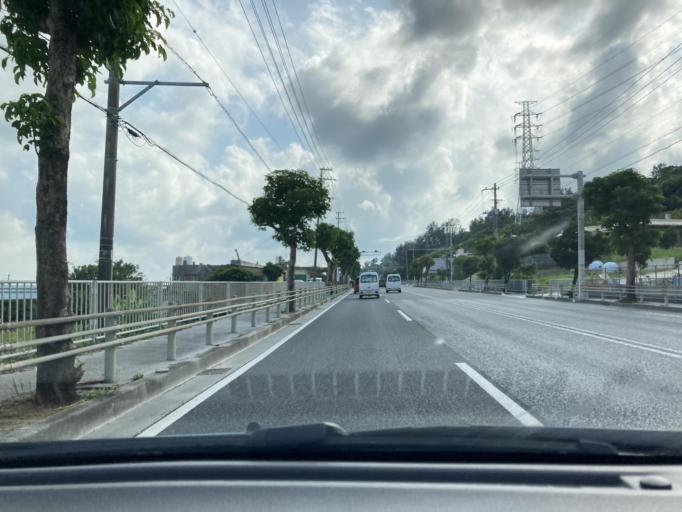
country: JP
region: Okinawa
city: Ginowan
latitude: 26.2530
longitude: 127.7840
